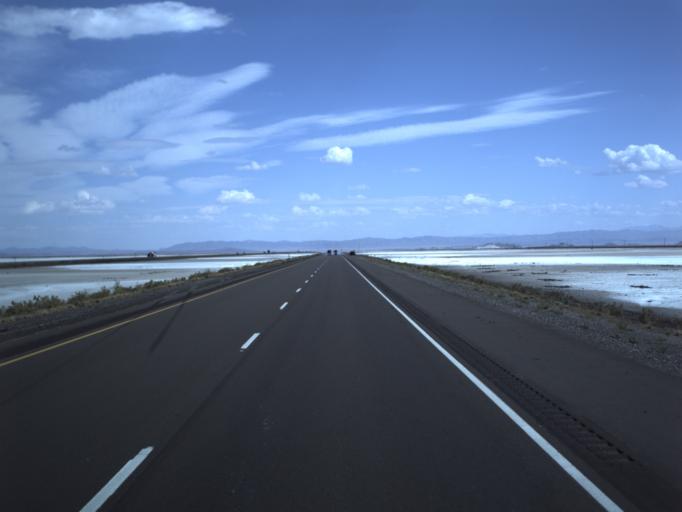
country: US
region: Utah
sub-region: Tooele County
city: Wendover
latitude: 40.7295
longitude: -113.4417
